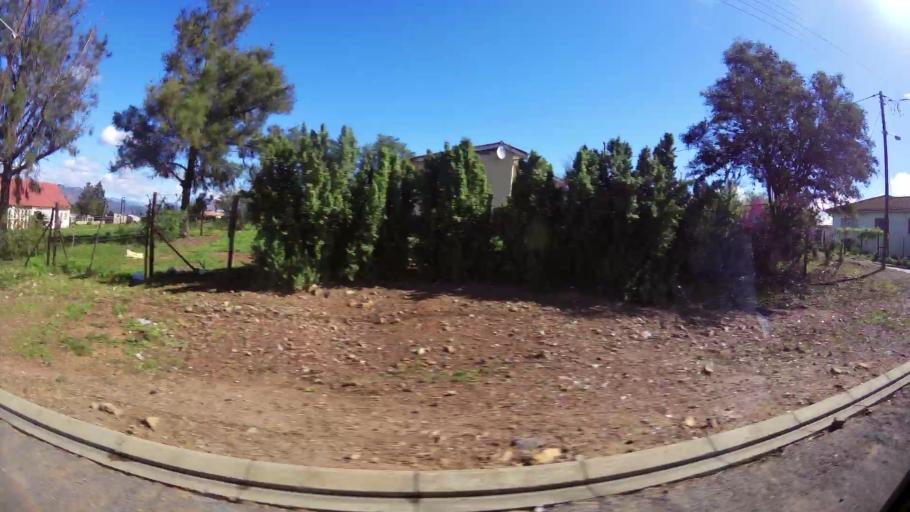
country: ZA
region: Western Cape
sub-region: Cape Winelands District Municipality
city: Ashton
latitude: -33.8342
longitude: 20.0460
